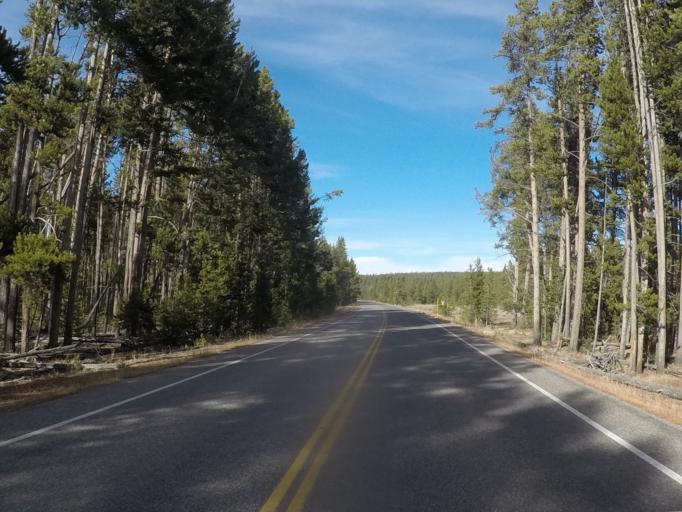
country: US
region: Montana
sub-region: Gallatin County
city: West Yellowstone
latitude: 44.5914
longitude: -110.8304
